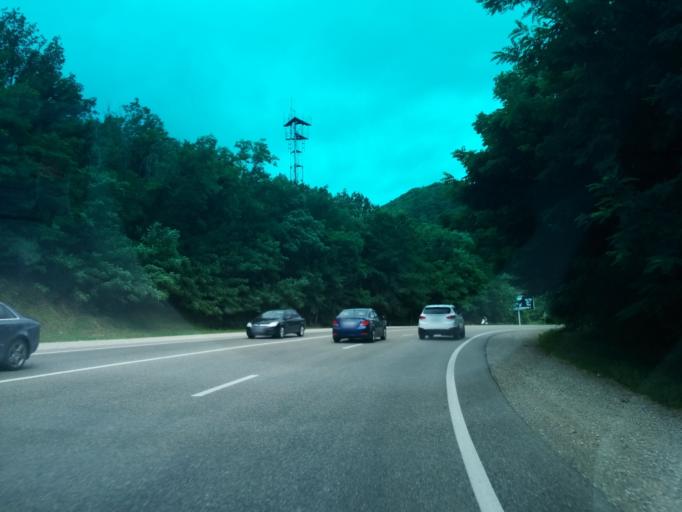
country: RU
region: Krasnodarskiy
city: Nebug
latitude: 44.1746
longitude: 38.9625
